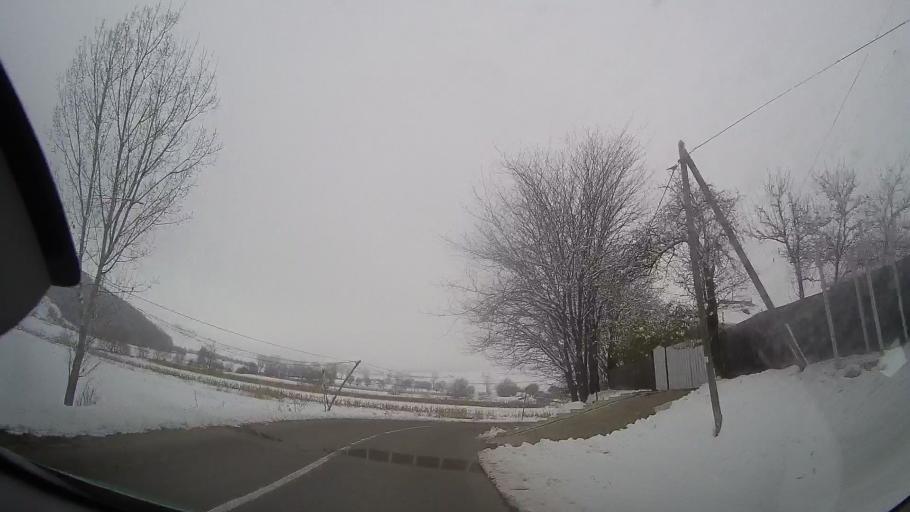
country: RO
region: Neamt
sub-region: Comuna Oniceni
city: Oniceni
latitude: 46.7996
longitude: 27.1415
